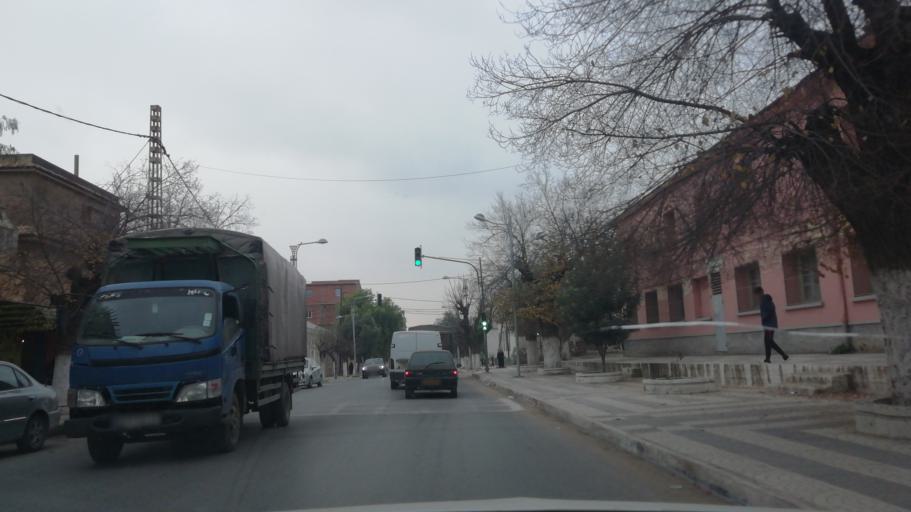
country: DZ
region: Sidi Bel Abbes
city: Sfizef
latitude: 35.2366
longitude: -0.2407
